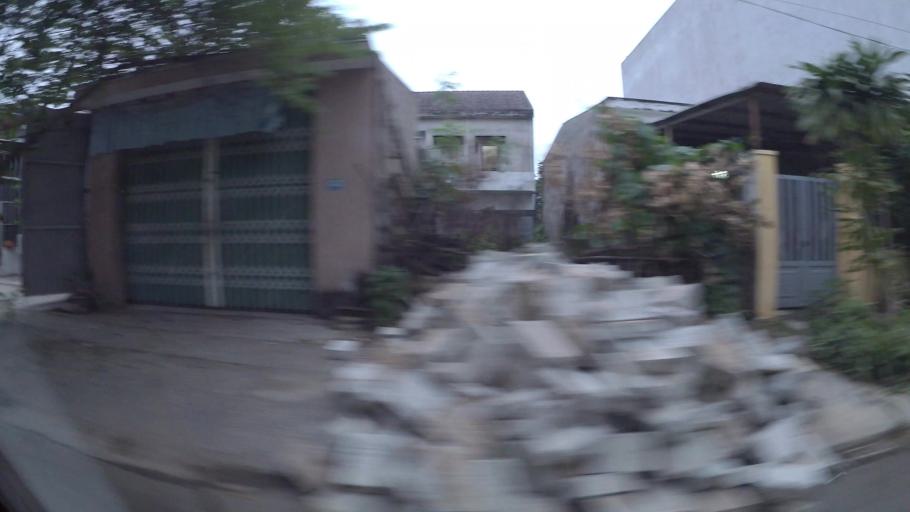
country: VN
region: Da Nang
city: Thanh Khe
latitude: 16.0513
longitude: 108.1770
